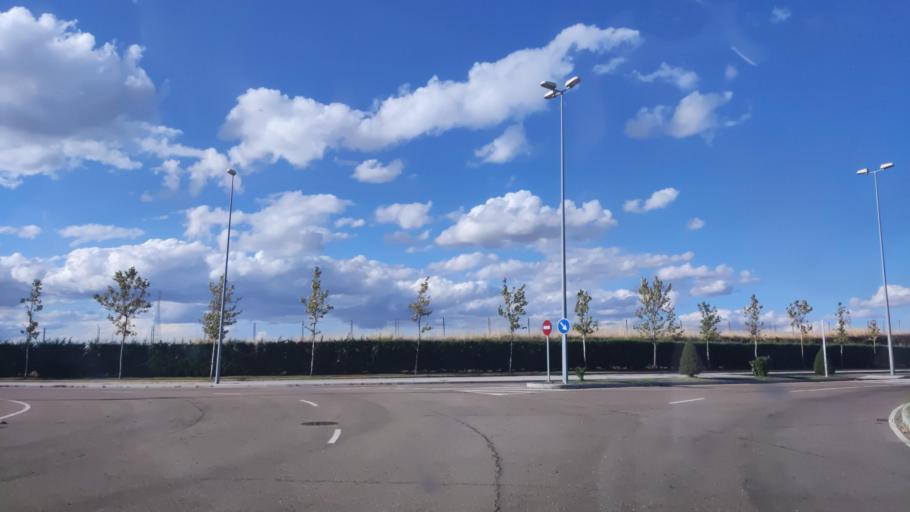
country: ES
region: Castille and Leon
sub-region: Provincia de Salamanca
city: Villamayor
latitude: 40.9688
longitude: -5.6948
